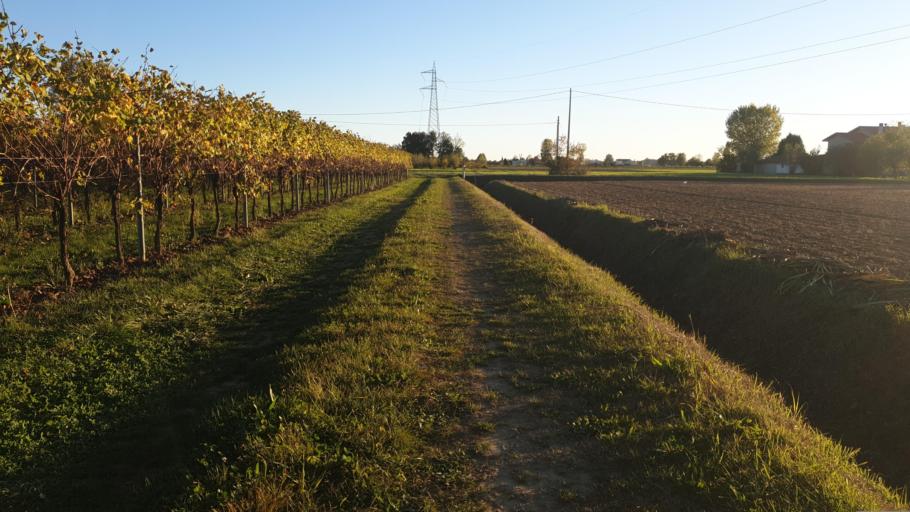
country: IT
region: Veneto
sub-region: Provincia di Venezia
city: Marano
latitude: 45.4491
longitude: 12.0990
